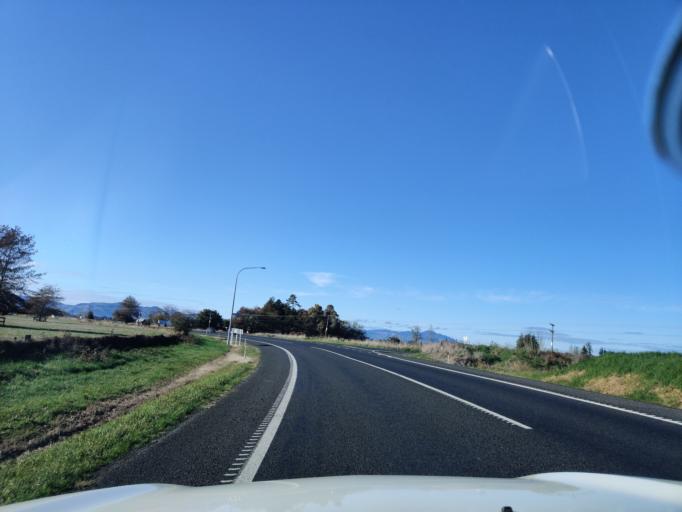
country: NZ
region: Waikato
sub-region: Hauraki District
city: Ngatea
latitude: -37.3100
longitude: 175.5653
